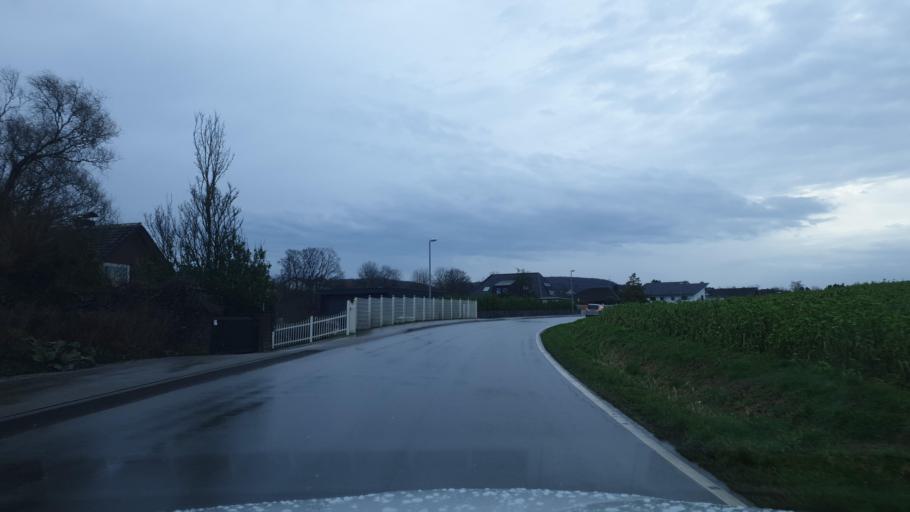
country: DE
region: North Rhine-Westphalia
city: Bad Oeynhausen
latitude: 52.1989
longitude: 8.8372
